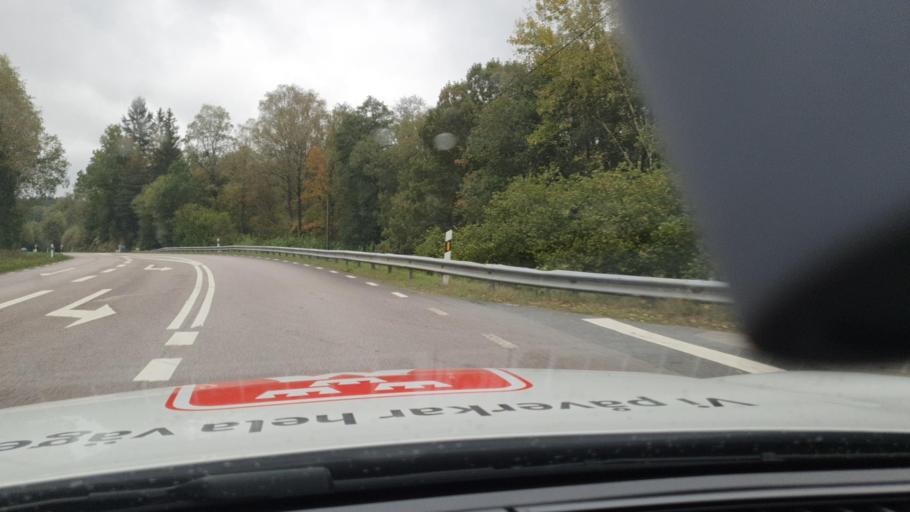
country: SE
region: Halland
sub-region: Falkenbergs Kommun
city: Falkenberg
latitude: 57.0961
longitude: 12.6745
